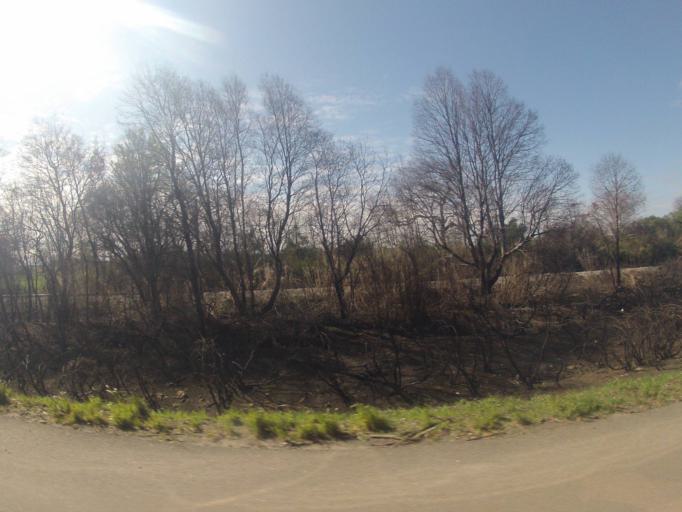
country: CL
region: Araucania
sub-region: Provincia de Malleco
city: Victoria
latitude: -38.1546
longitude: -72.3069
